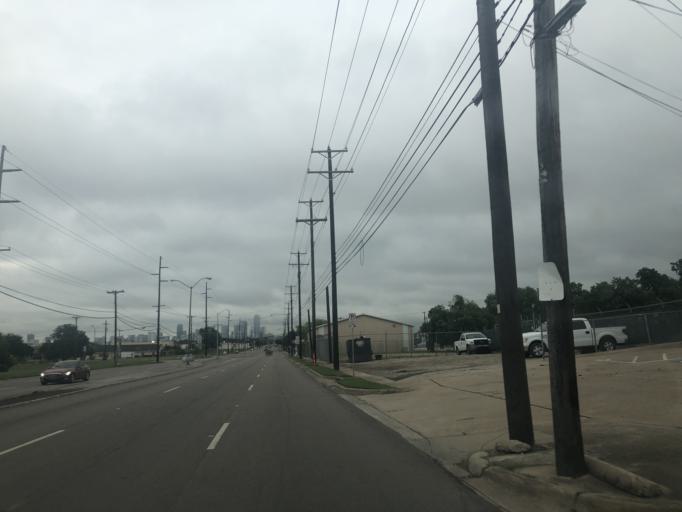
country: US
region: Texas
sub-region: Dallas County
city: Cockrell Hill
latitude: 32.7786
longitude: -96.8672
